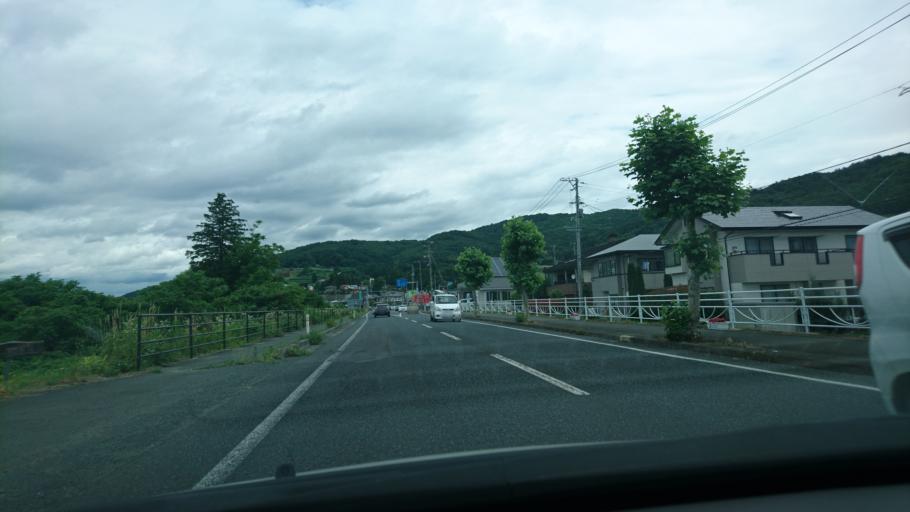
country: JP
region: Iwate
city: Morioka-shi
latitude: 39.6545
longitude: 141.1823
